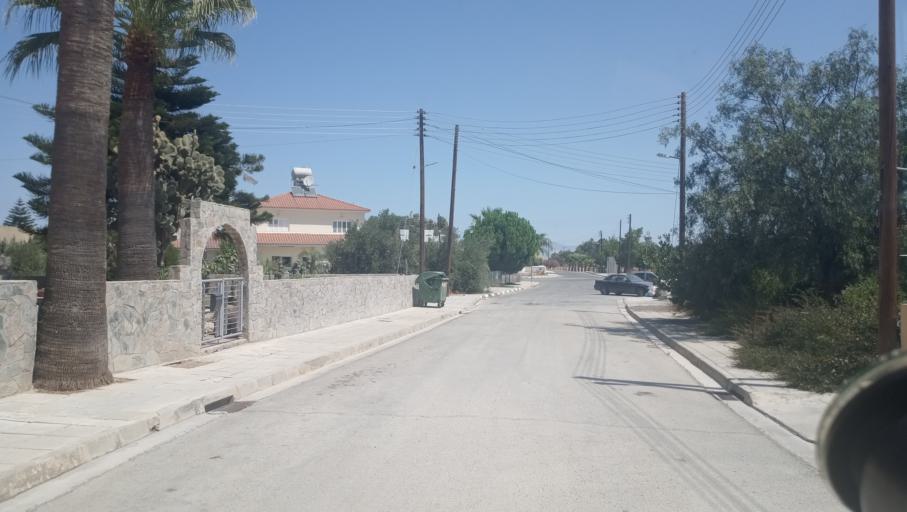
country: CY
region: Lefkosia
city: Psimolofou
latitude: 35.0609
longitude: 33.2638
